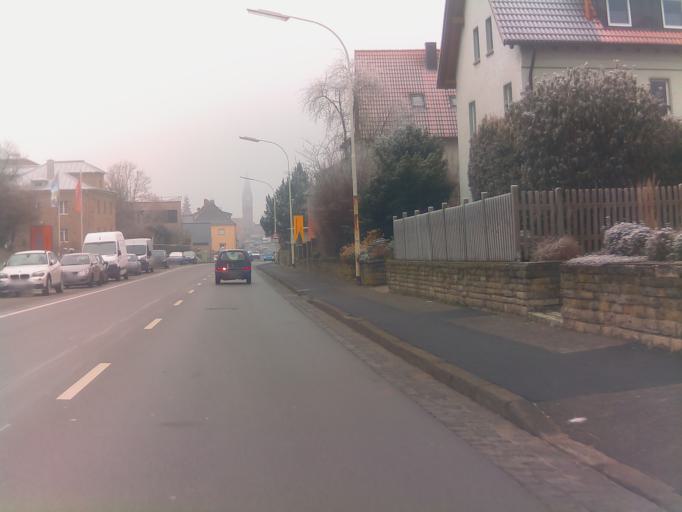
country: DE
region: Bavaria
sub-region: Regierungsbezirk Unterfranken
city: Hassfurt
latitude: 50.0369
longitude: 10.5150
